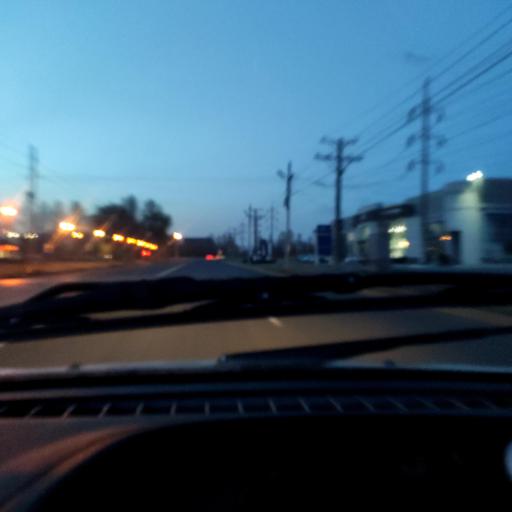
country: RU
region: Samara
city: Tol'yatti
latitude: 53.5553
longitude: 49.2937
